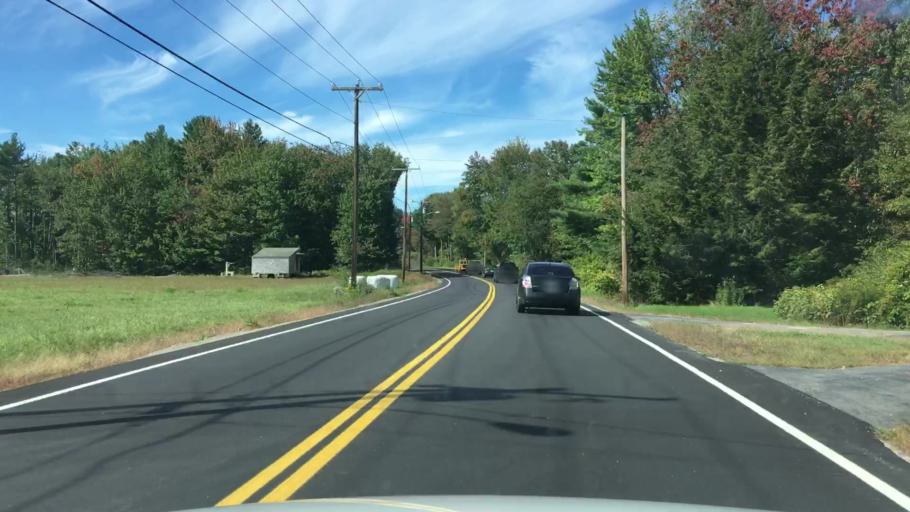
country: US
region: Maine
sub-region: York County
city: Biddeford
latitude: 43.5429
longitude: -70.4965
